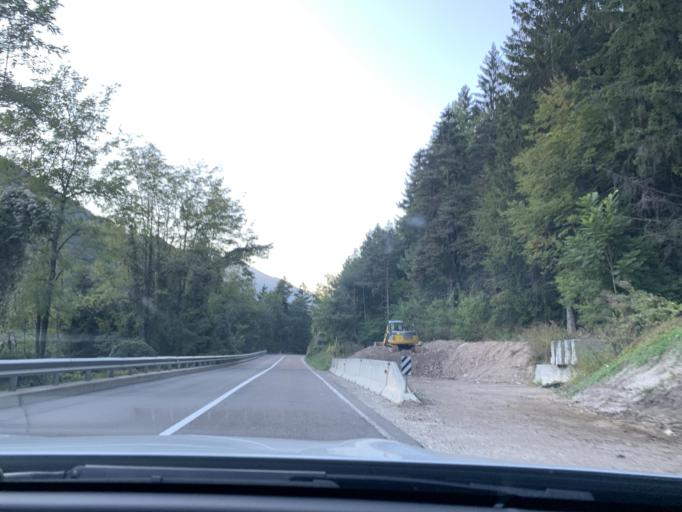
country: IT
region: Trentino-Alto Adige
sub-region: Bolzano
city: Nova Ponente
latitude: 46.4431
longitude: 11.4632
